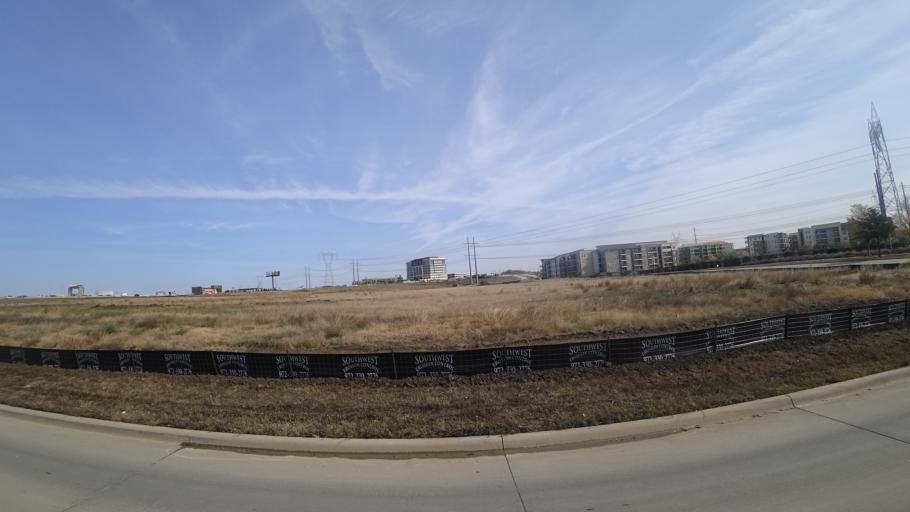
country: US
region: Texas
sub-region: Denton County
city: The Colony
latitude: 33.0579
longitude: -96.9003
